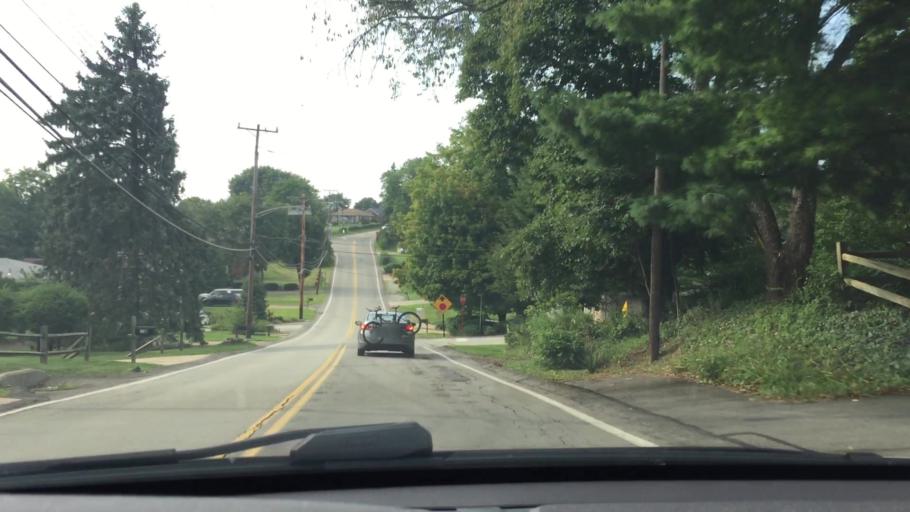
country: US
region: Pennsylvania
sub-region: Allegheny County
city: Pitcairn
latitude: 40.4212
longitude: -79.7479
